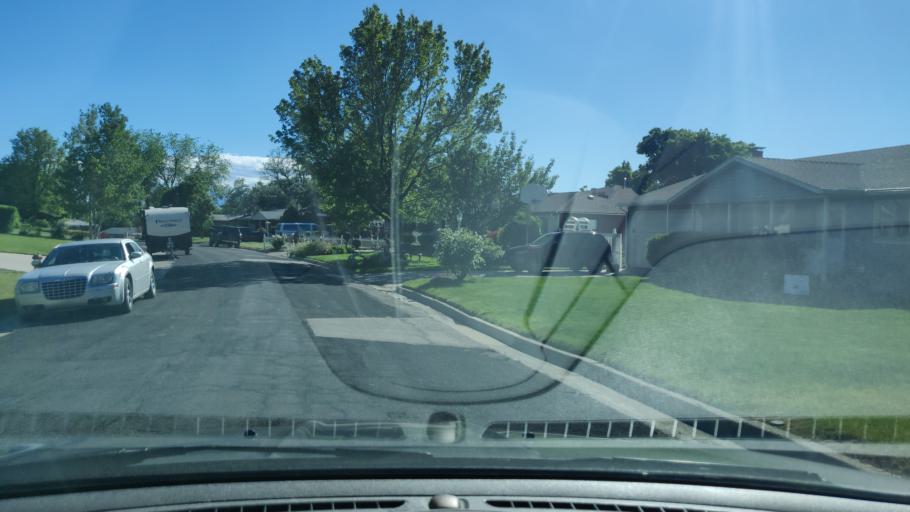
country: US
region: Utah
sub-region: Salt Lake County
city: Cottonwood Heights
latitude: 40.6115
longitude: -111.8119
